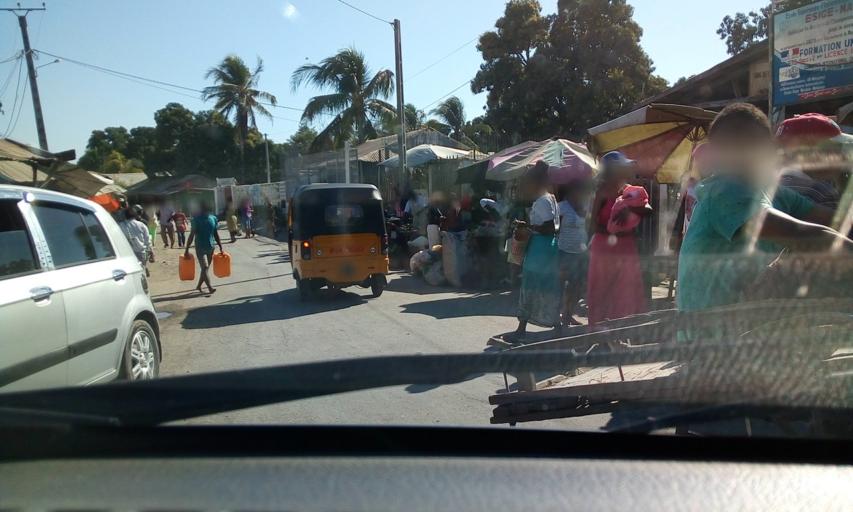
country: MG
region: Boeny
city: Mahajanga
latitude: -15.7143
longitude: 46.3388
